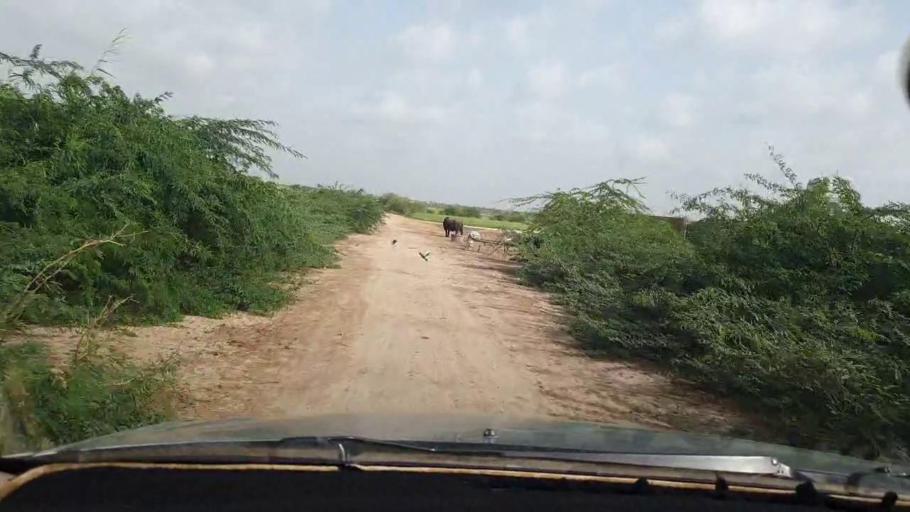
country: PK
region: Sindh
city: Tando Bago
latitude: 24.7823
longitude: 68.9790
